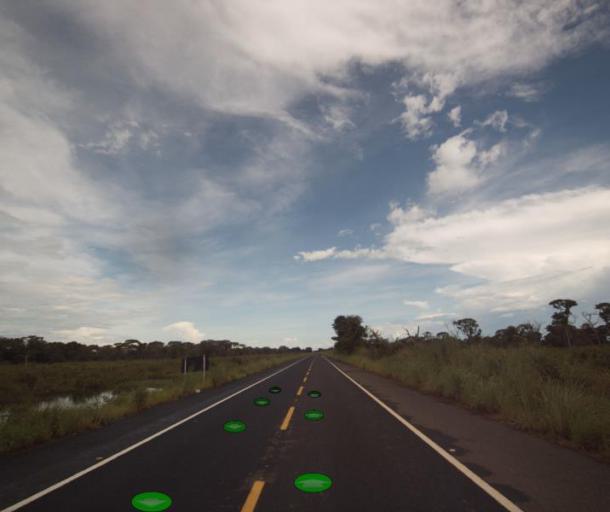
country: BR
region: Goias
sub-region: Sao Miguel Do Araguaia
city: Sao Miguel do Araguaia
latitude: -13.2232
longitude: -50.5707
